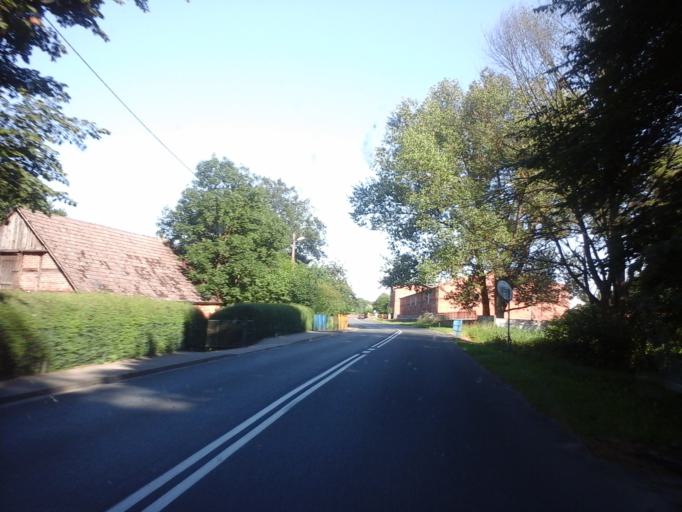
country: PL
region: West Pomeranian Voivodeship
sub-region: Powiat goleniowski
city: Nowogard
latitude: 53.6497
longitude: 15.2187
